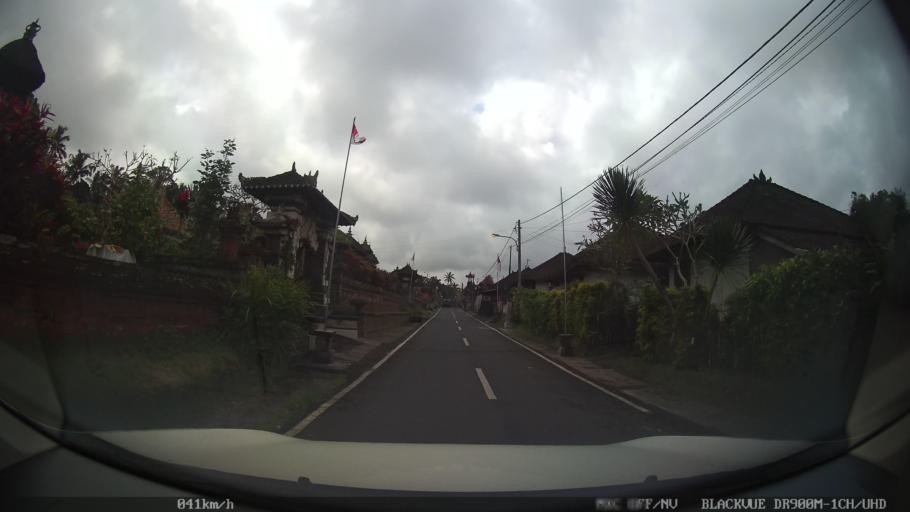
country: ID
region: Bali
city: Pemijian
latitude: -8.4495
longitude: 115.2285
